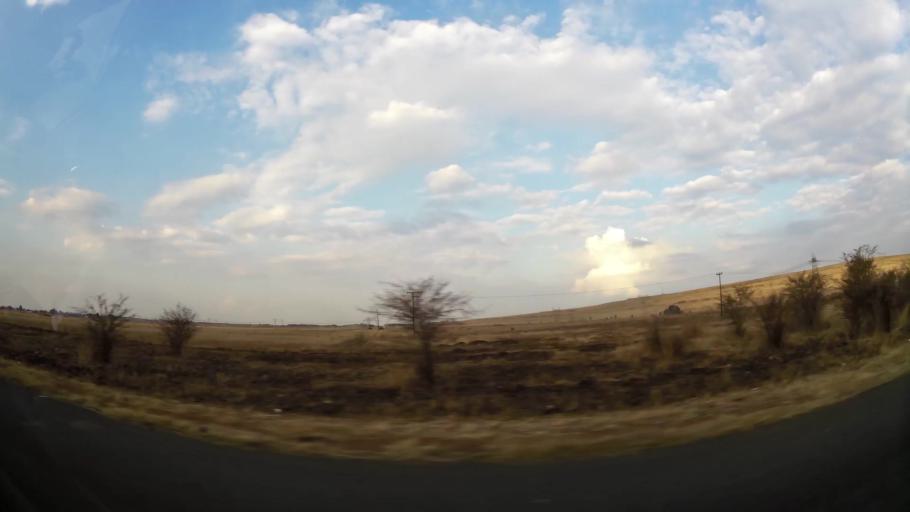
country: ZA
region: Gauteng
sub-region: Sedibeng District Municipality
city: Vanderbijlpark
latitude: -26.6296
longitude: 27.8093
